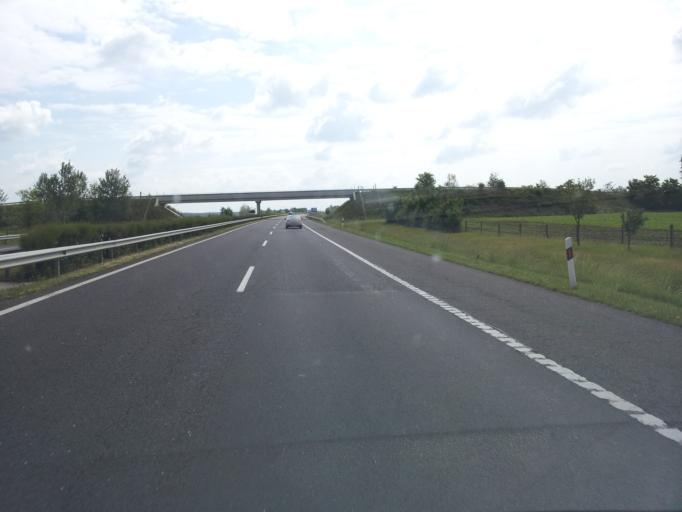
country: HU
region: Borsod-Abauj-Zemplen
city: Emod
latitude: 47.8848
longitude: 20.8597
